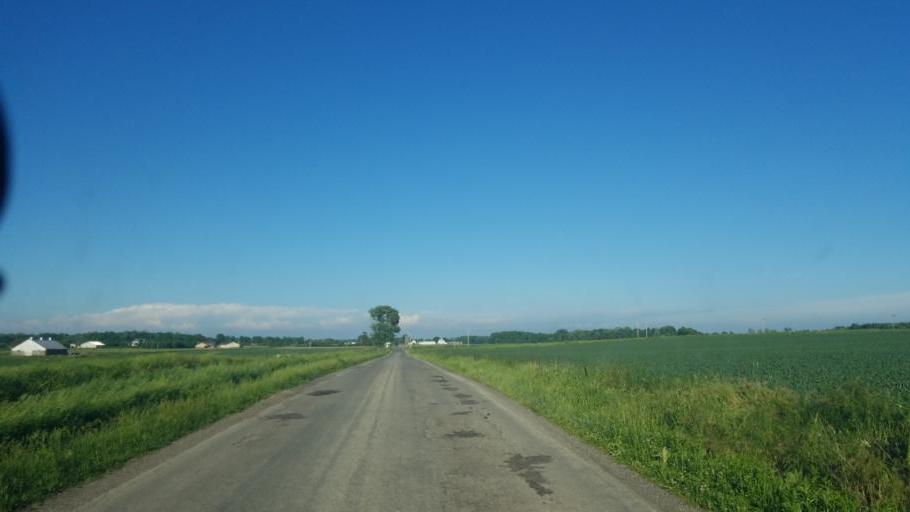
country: US
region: Indiana
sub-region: Marshall County
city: Bremen
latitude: 41.4265
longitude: -86.0867
